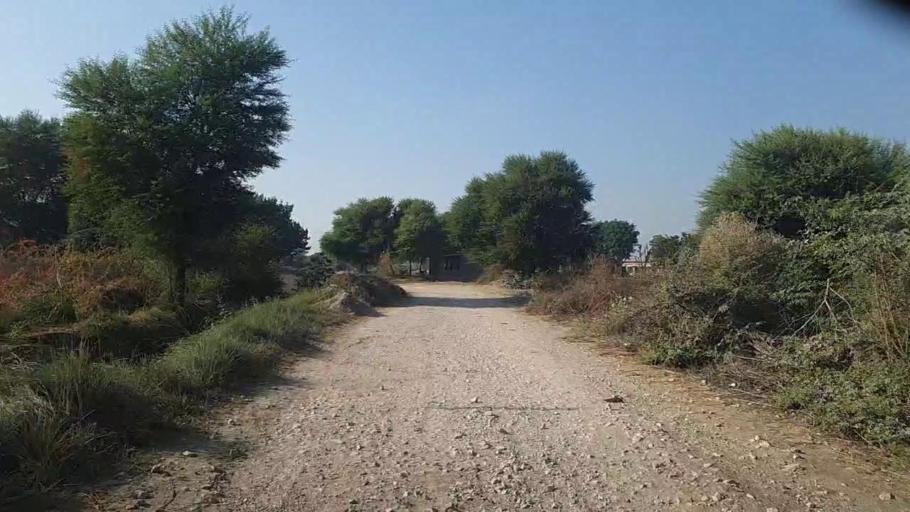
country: PK
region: Sindh
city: Darya Khan Marri
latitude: 26.6787
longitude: 68.3716
